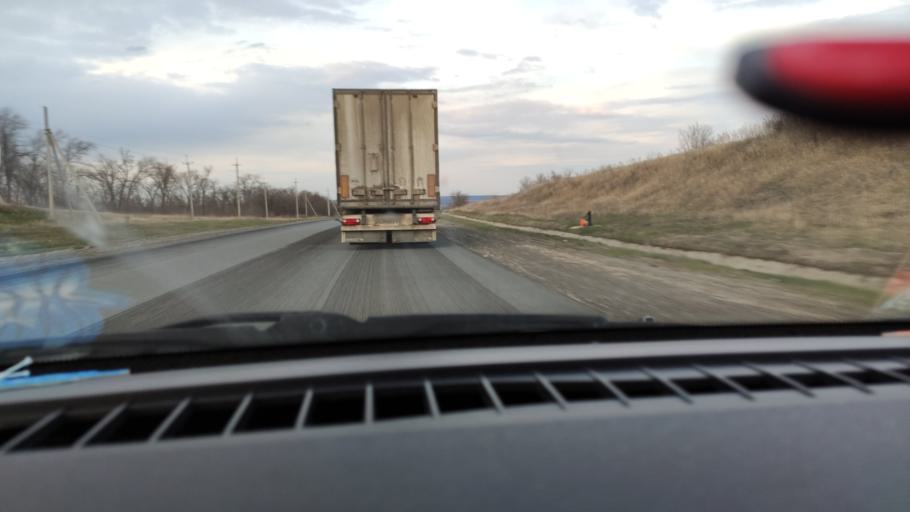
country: RU
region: Saratov
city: Shumeyka
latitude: 51.7877
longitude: 46.1429
